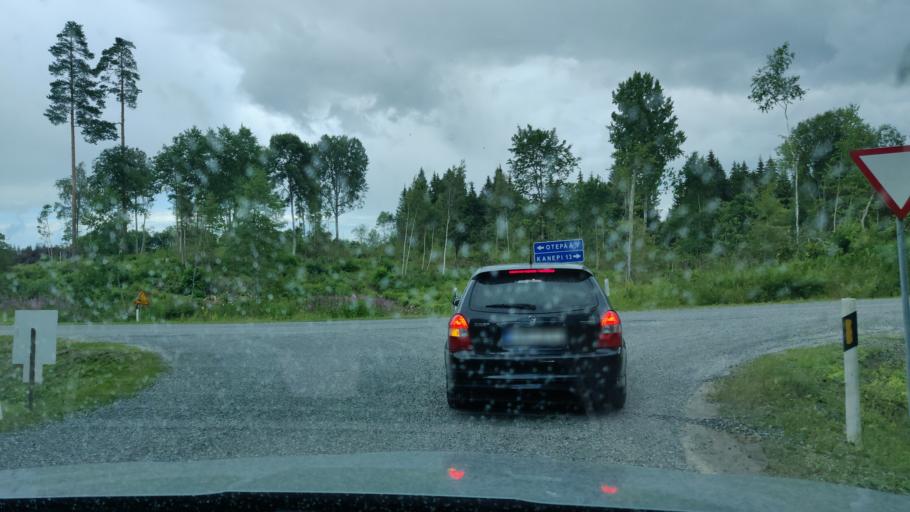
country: EE
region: Vorumaa
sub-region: Antsla vald
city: Vana-Antsla
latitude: 58.0222
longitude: 26.5808
